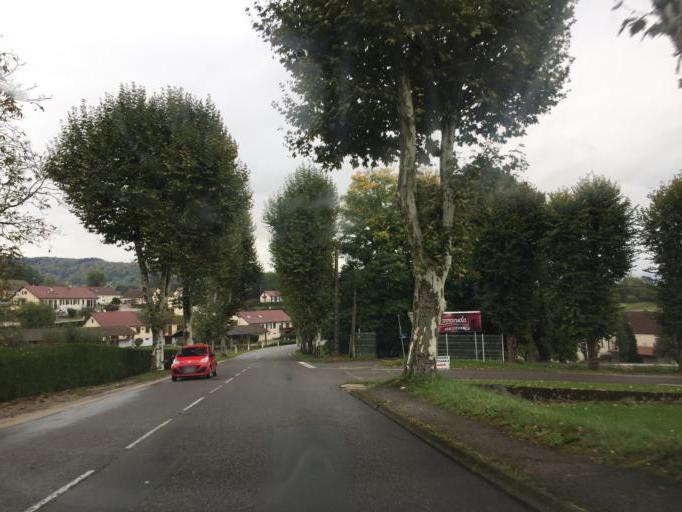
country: FR
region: Franche-Comte
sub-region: Departement du Jura
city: Orgelet
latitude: 46.5236
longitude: 5.6170
